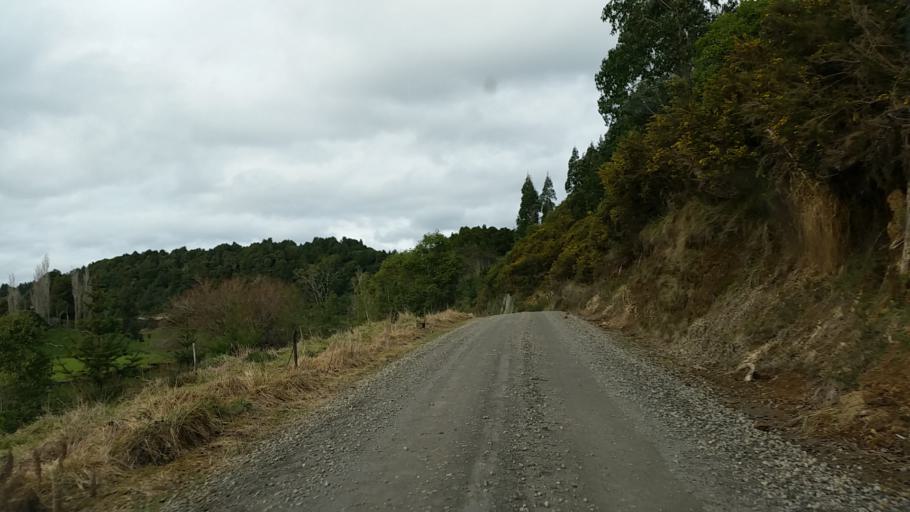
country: NZ
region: Taranaki
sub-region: New Plymouth District
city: Waitara
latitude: -39.1564
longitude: 174.5256
